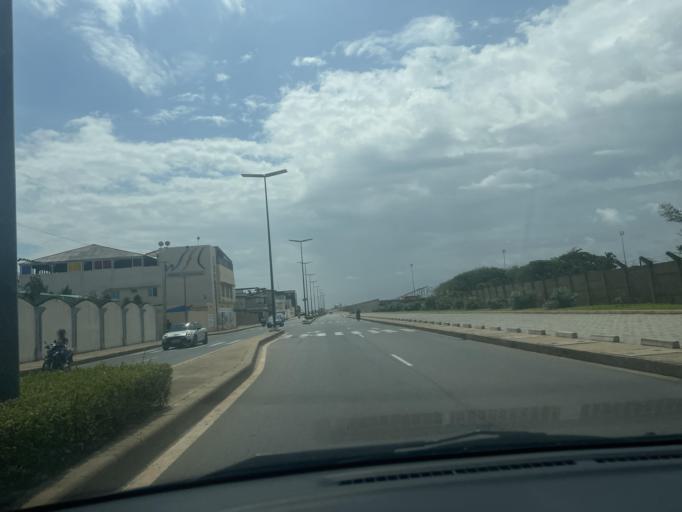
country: BJ
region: Littoral
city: Cotonou
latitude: 6.3497
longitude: 2.3830
